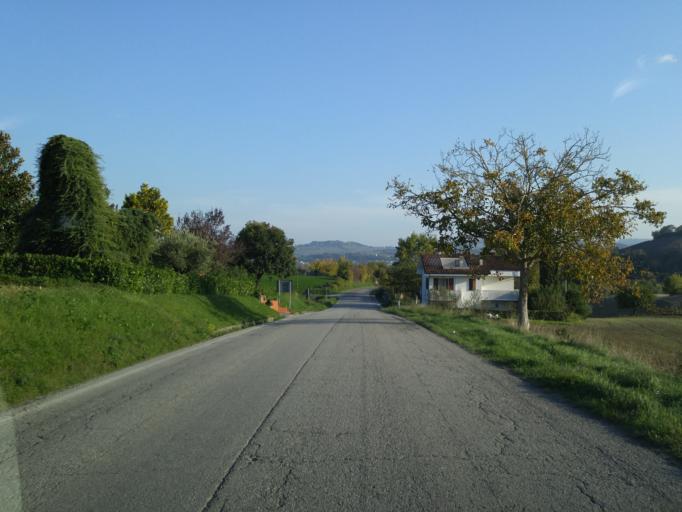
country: IT
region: The Marches
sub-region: Provincia di Pesaro e Urbino
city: Montefelcino
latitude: 43.7217
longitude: 12.8420
